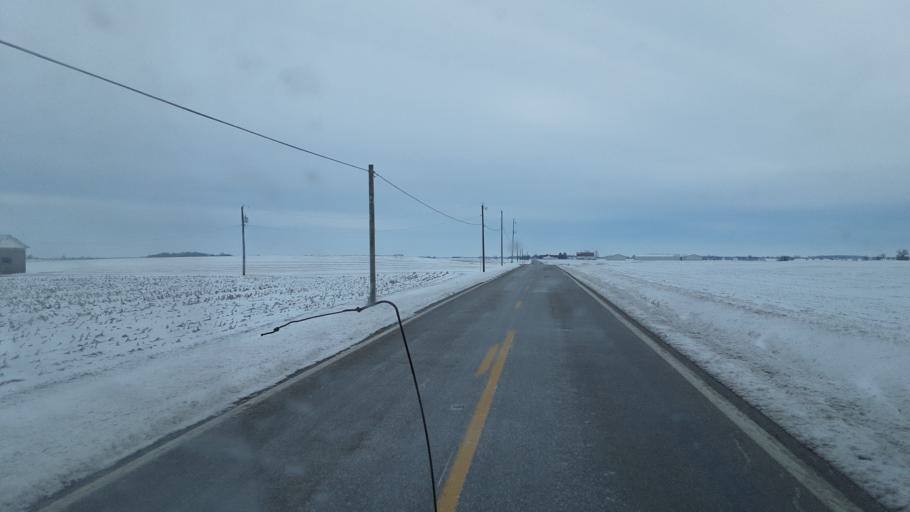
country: US
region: Ohio
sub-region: Madison County
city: Bethel
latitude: 39.7328
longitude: -83.4588
